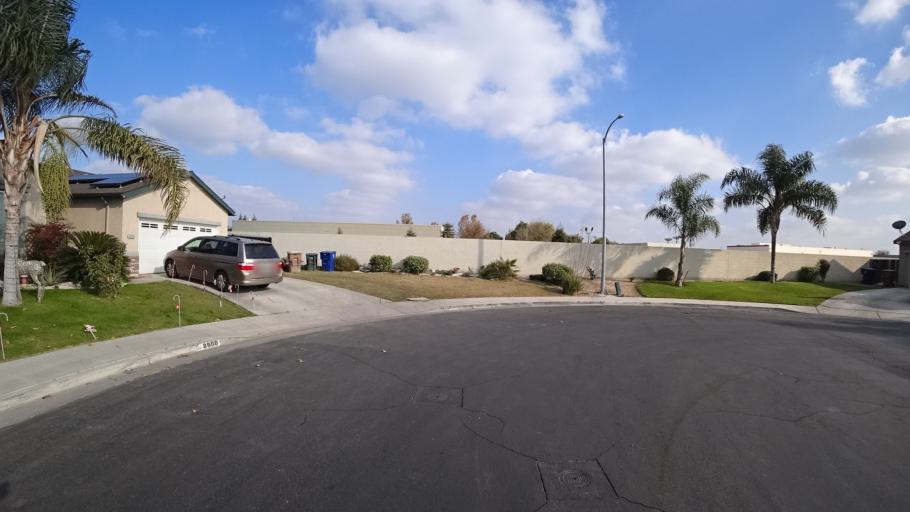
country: US
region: California
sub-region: Kern County
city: Greenacres
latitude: 35.3071
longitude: -119.1016
